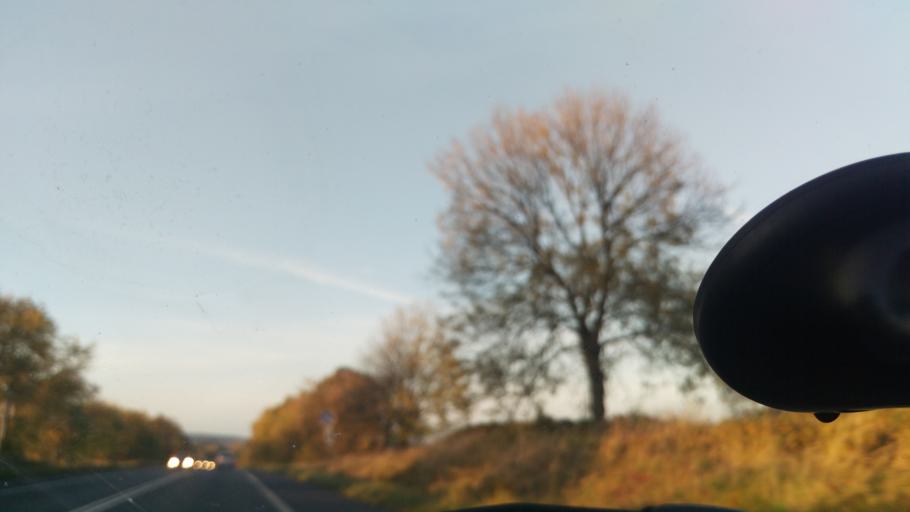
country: PL
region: West Pomeranian Voivodeship
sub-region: Powiat gryfinski
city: Stare Czarnowo
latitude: 53.2660
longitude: 14.7835
